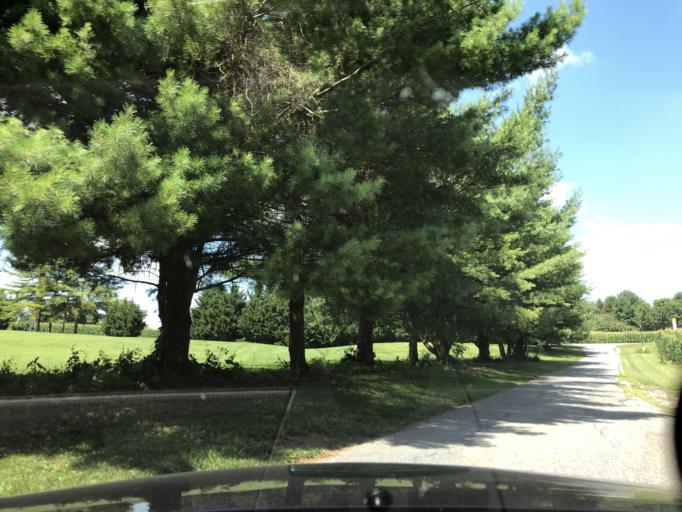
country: US
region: Maryland
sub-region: Carroll County
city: Westminster
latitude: 39.6020
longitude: -76.9668
